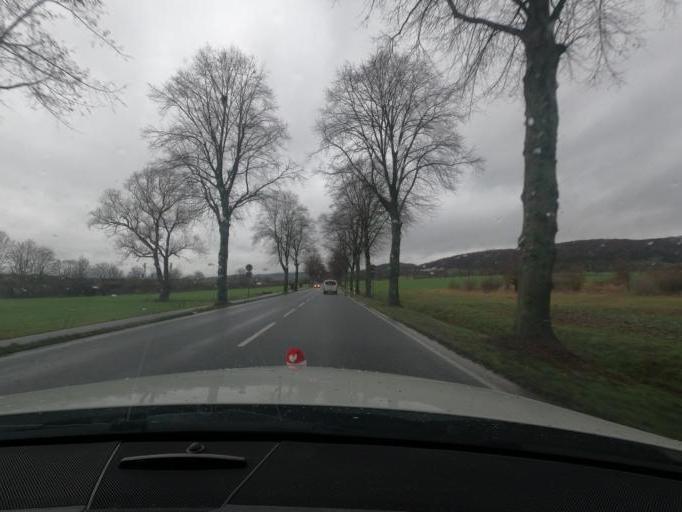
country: DE
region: Lower Saxony
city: Einbeck
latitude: 51.7835
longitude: 9.9350
